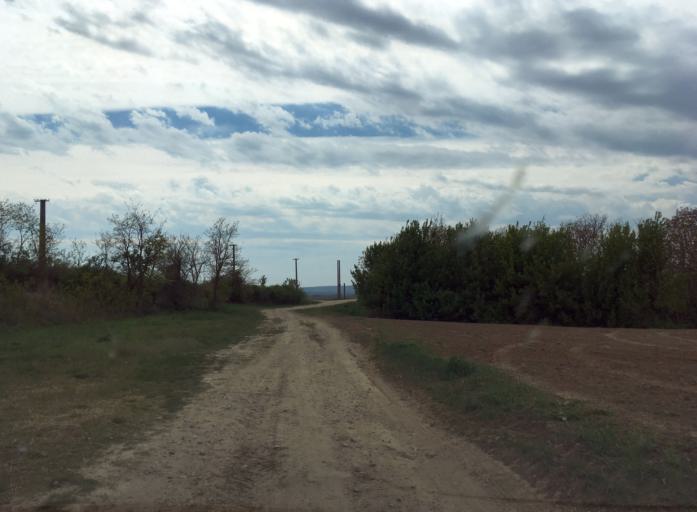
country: SK
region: Nitriansky
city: Svodin
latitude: 47.9210
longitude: 18.4173
